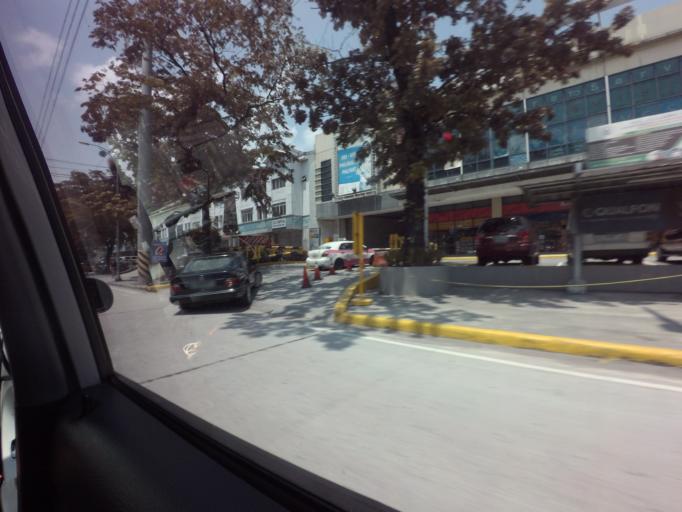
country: PH
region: Metro Manila
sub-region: City of Manila
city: Quiapo
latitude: 14.5878
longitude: 120.9960
